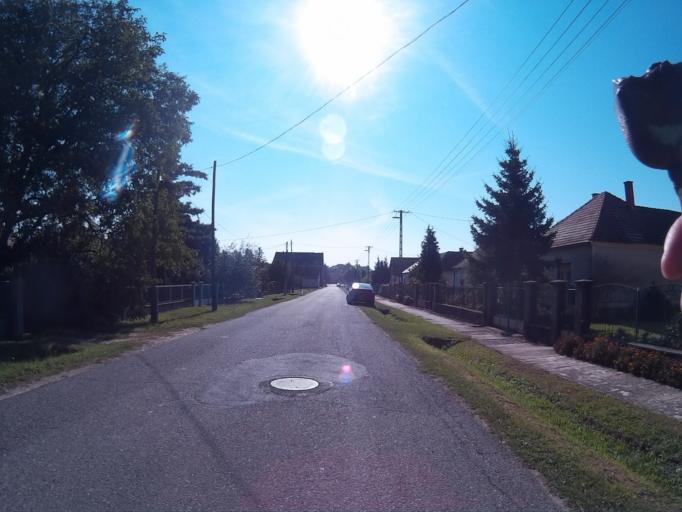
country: HU
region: Vas
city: Jak
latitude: 47.0898
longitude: 16.6218
